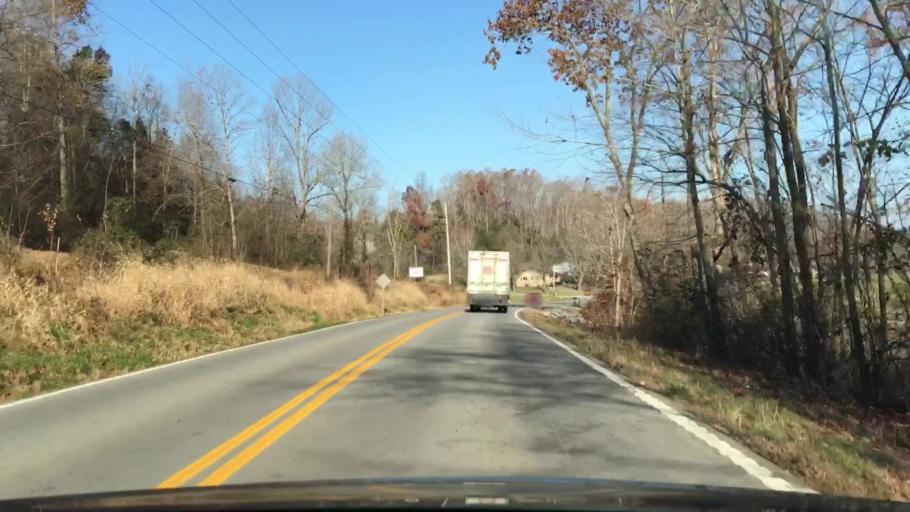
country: US
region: Kentucky
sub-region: Grayson County
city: Leitchfield
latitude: 37.4461
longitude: -86.2893
